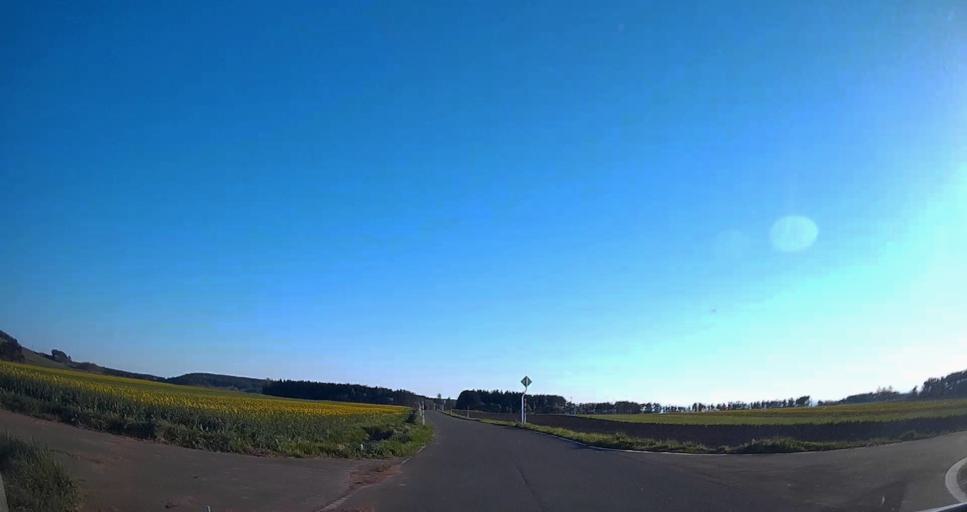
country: JP
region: Aomori
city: Mutsu
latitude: 41.1163
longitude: 141.2745
